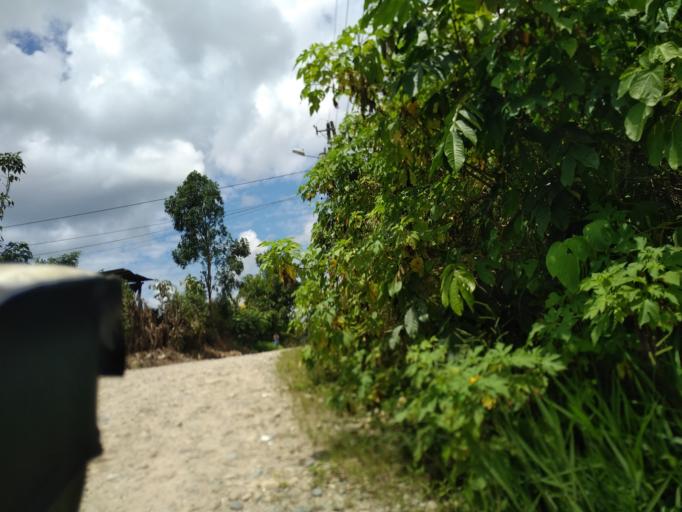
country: EC
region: Napo
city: Tena
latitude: -0.9922
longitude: -77.8242
